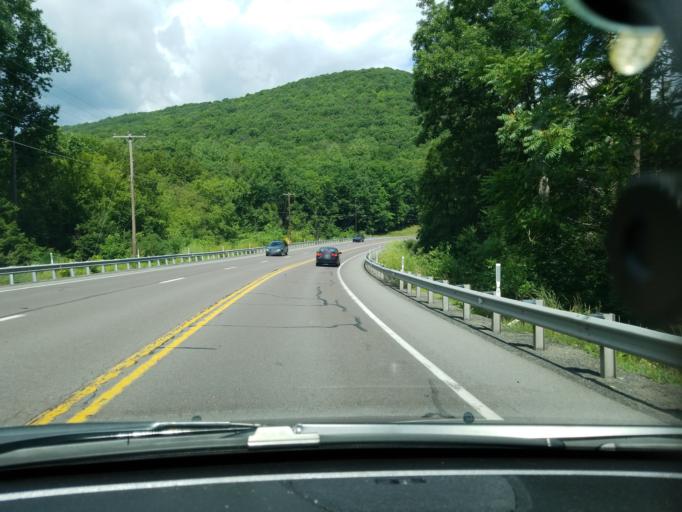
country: US
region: Pennsylvania
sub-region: Northumberland County
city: Kulpmont
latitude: 40.8229
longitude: -76.5010
